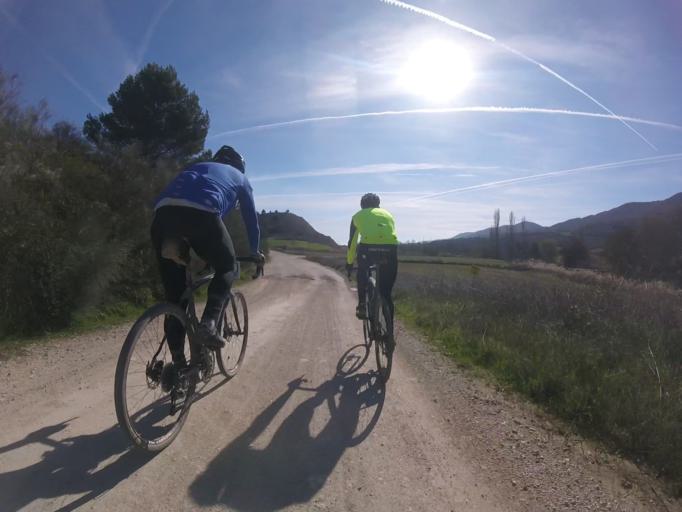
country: ES
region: Navarre
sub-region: Provincia de Navarra
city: Cirauqui
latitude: 42.6735
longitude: -1.9128
